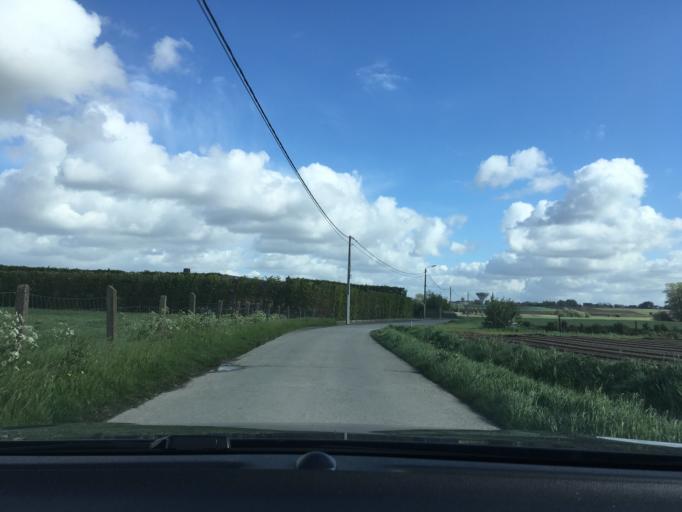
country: BE
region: Flanders
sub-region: Provincie West-Vlaanderen
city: Hooglede
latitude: 50.9935
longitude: 3.0739
